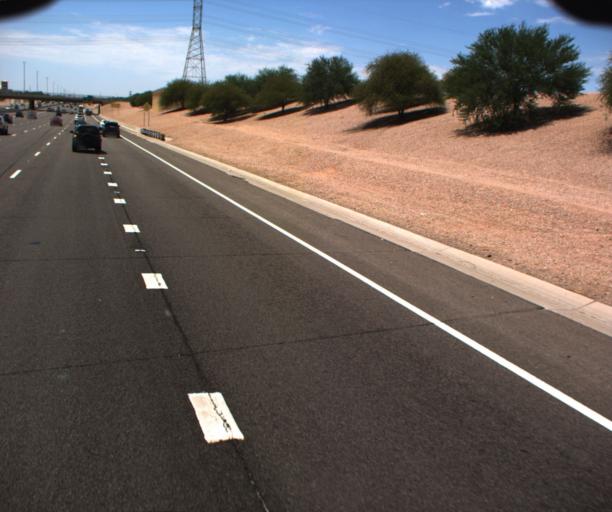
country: US
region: Arizona
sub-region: Maricopa County
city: Gilbert
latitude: 33.3867
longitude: -111.7436
